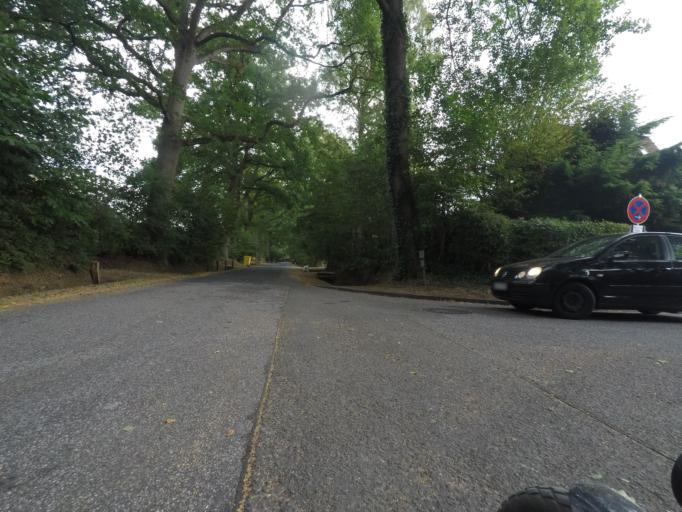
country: DE
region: Hamburg
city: Bergstedt
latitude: 53.6408
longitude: 10.1453
